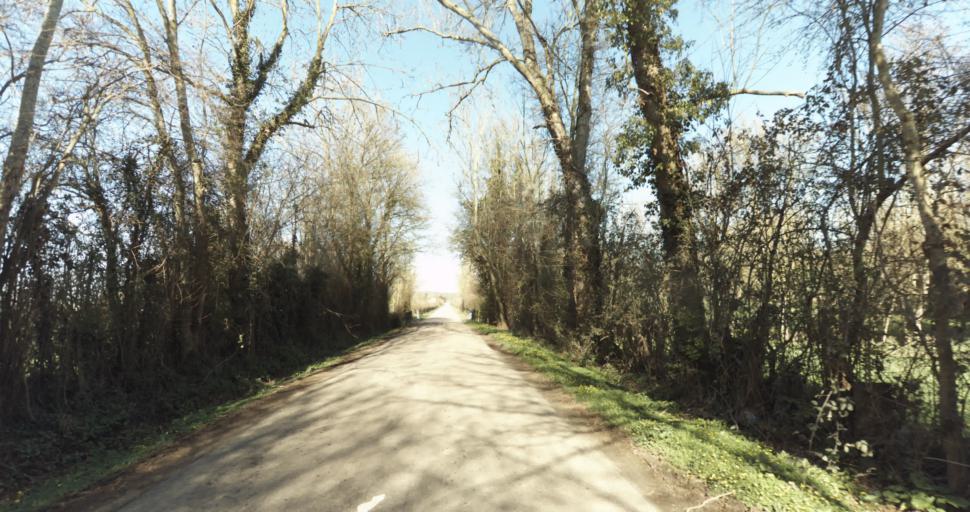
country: FR
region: Lower Normandy
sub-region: Departement du Calvados
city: Saint-Pierre-sur-Dives
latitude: 48.9711
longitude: 0.0471
